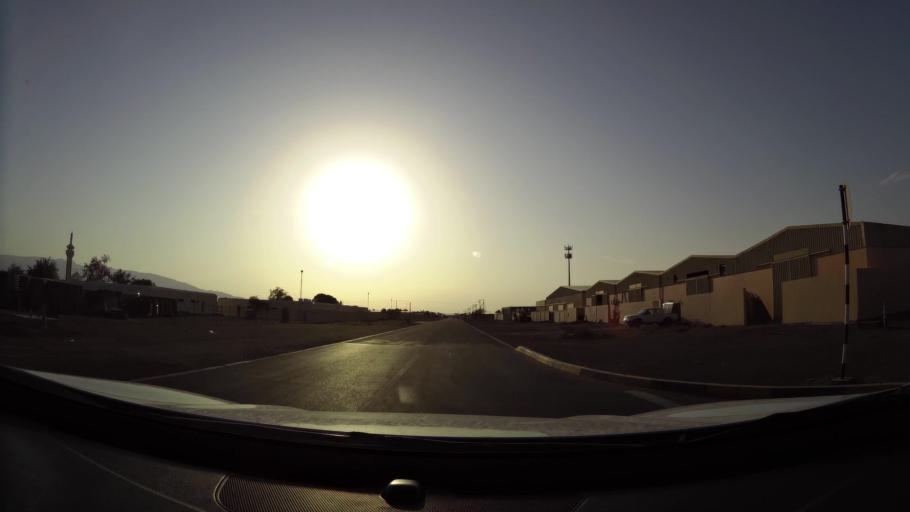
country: AE
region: Abu Dhabi
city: Al Ain
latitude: 24.1453
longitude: 55.8435
